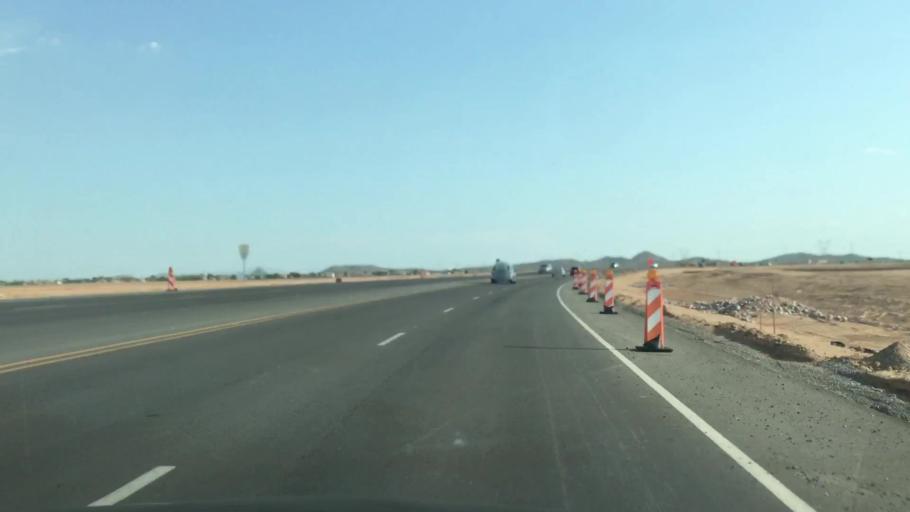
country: US
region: Arizona
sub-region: Pinal County
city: San Tan Valley
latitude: 33.1539
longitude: -111.5445
